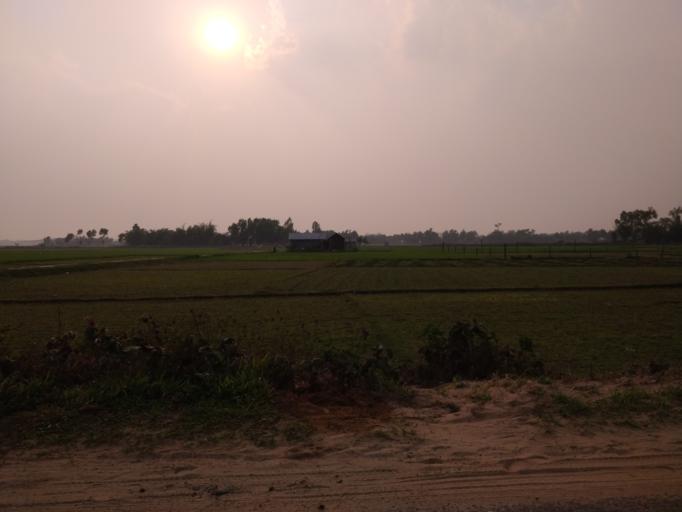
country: BD
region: Sylhet
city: Habiganj
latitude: 24.1421
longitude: 91.3511
